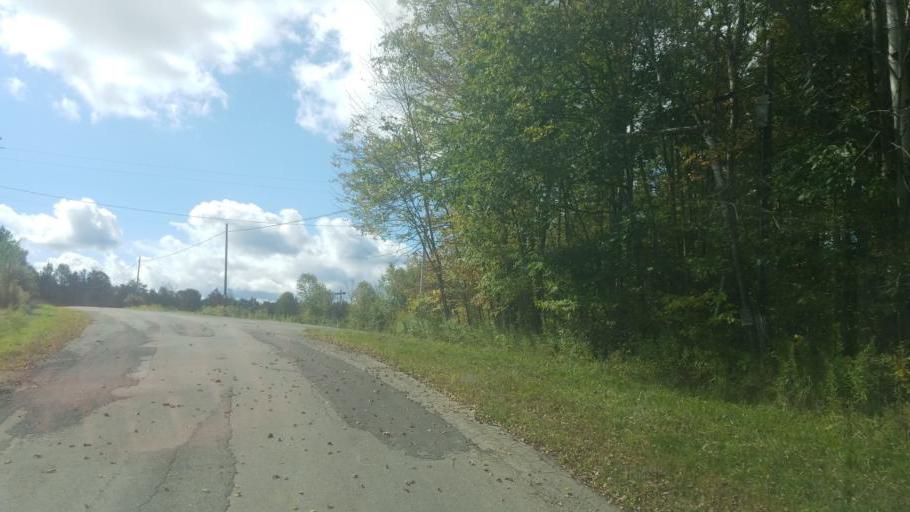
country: US
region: New York
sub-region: Cattaraugus County
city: Franklinville
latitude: 42.2279
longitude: -78.4154
